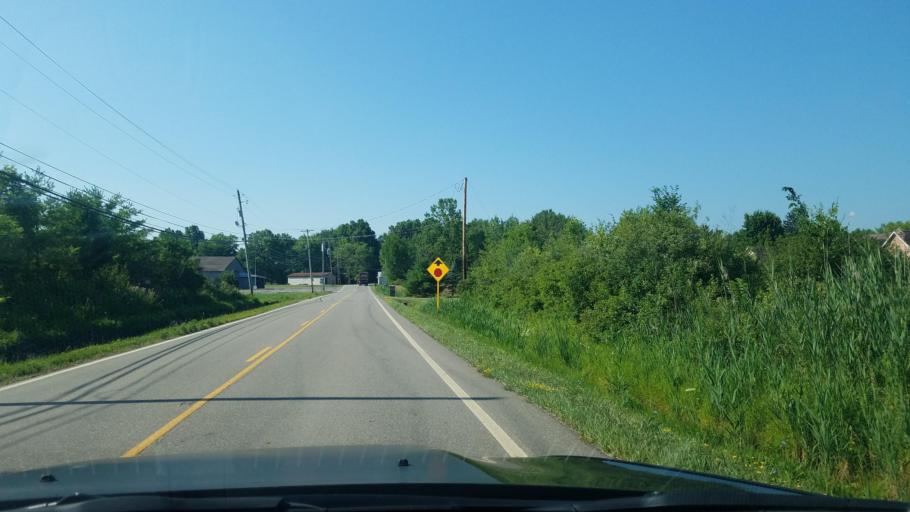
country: US
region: Ohio
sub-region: Trumbull County
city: Champion Heights
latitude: 41.3028
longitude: -80.8979
